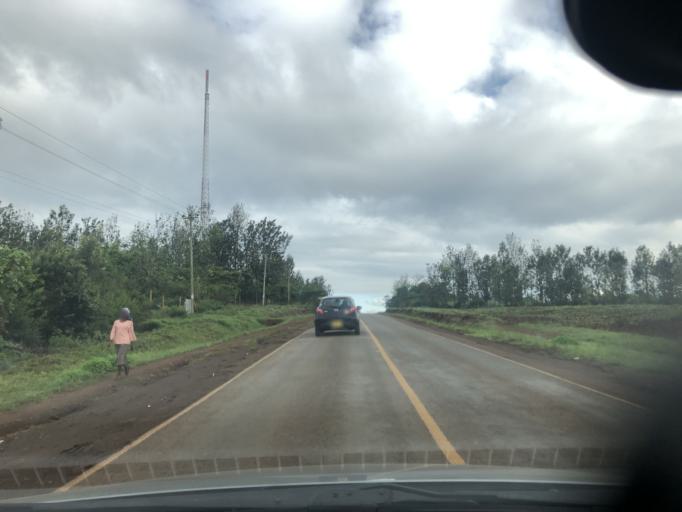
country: KE
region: Murang'a District
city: Maragua
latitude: -0.8357
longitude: 37.1377
